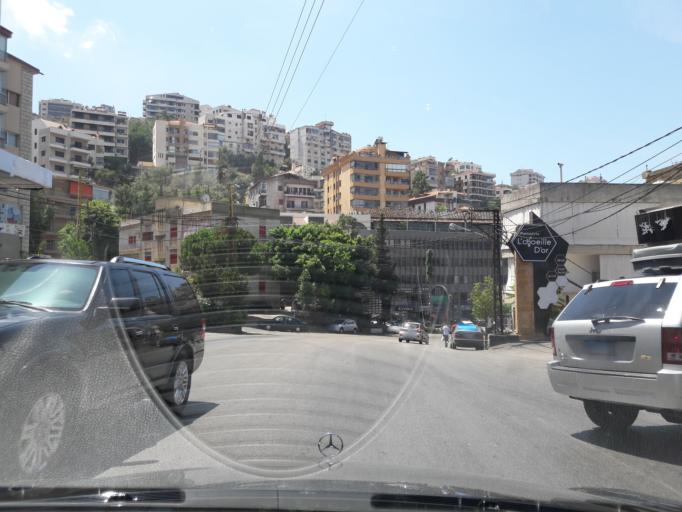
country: LB
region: Mont-Liban
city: Djounie
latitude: 33.9255
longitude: 35.6340
